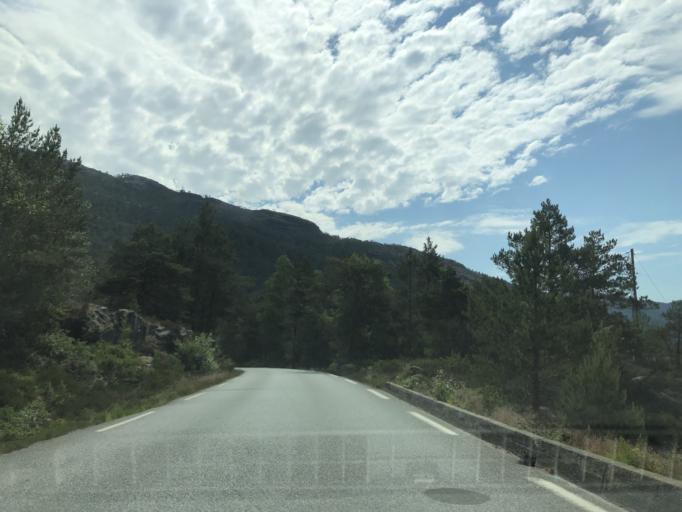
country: NO
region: Hordaland
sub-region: Jondal
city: Jondal
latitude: 60.3284
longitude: 6.3382
